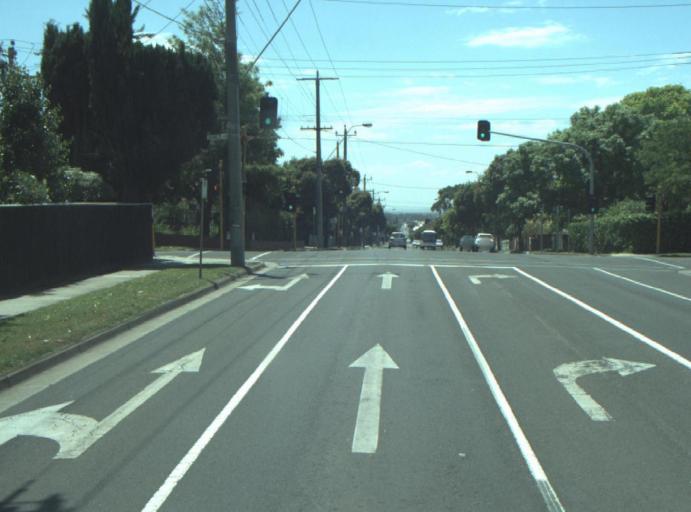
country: AU
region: Victoria
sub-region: Greater Geelong
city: Geelong West
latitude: -38.1530
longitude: 144.3340
